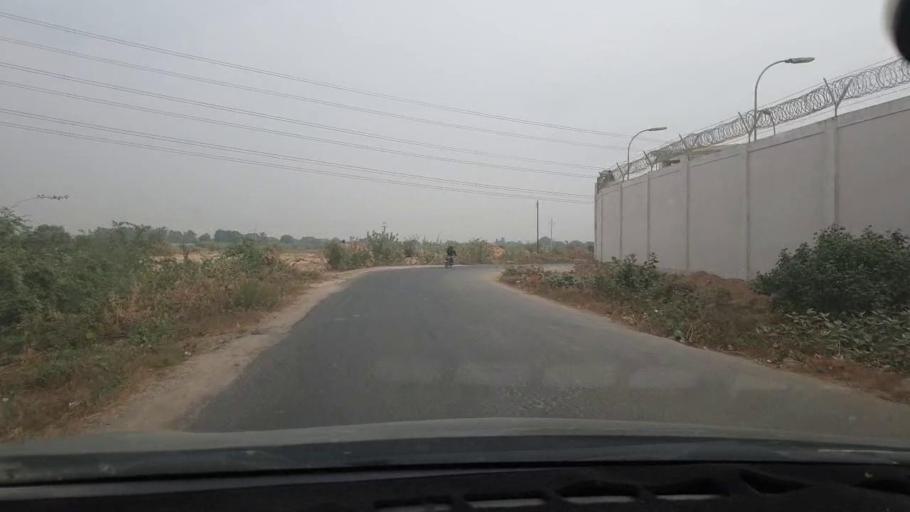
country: PK
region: Sindh
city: Malir Cantonment
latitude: 24.9117
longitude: 67.2824
